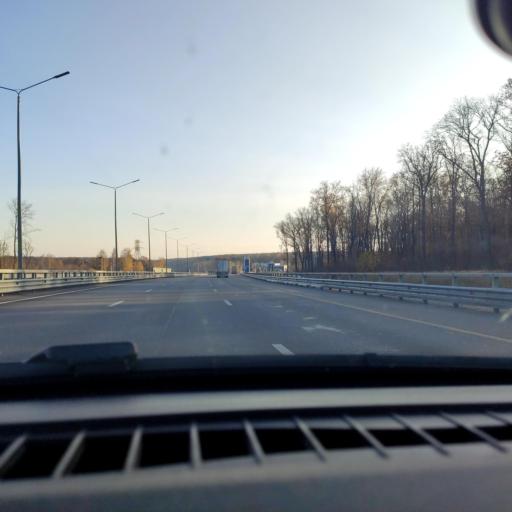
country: RU
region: Voronezj
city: Podgornoye
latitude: 51.8155
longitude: 39.2519
